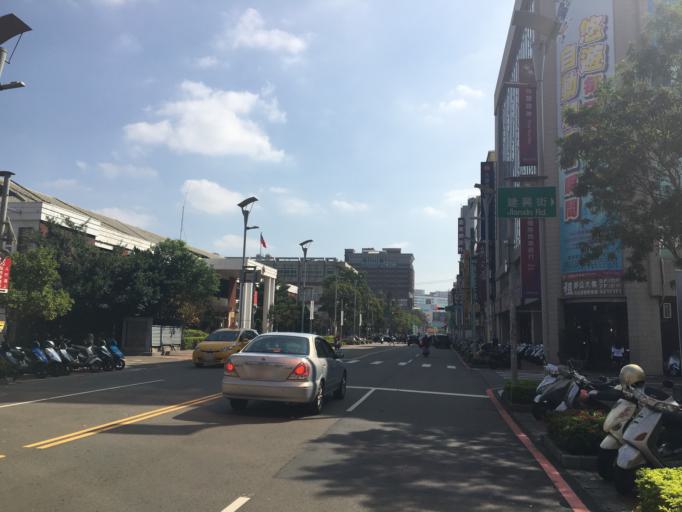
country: TW
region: Taiwan
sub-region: Hsinchu
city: Hsinchu
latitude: 24.8086
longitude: 120.9672
